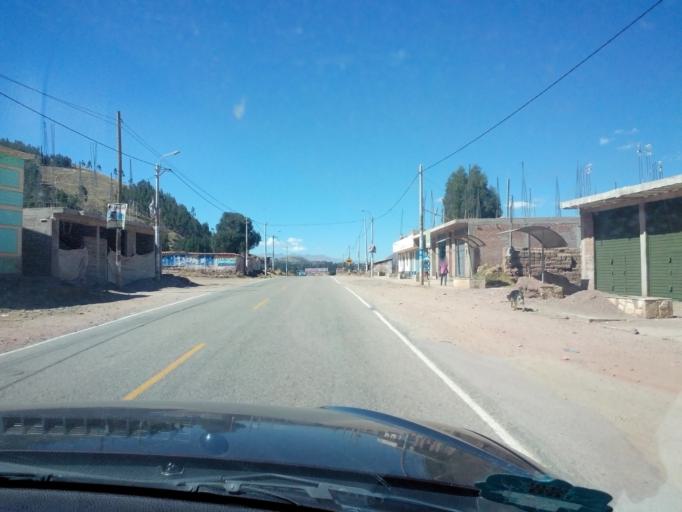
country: PE
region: Cusco
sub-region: Provincia de Canchis
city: Tinta
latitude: -14.1422
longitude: -71.4007
